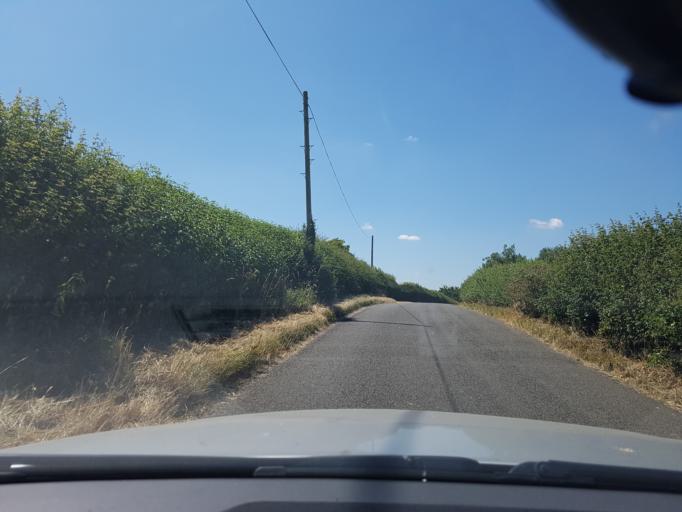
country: GB
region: England
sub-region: Northamptonshire
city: Deanshanger
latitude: 52.0211
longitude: -0.8903
